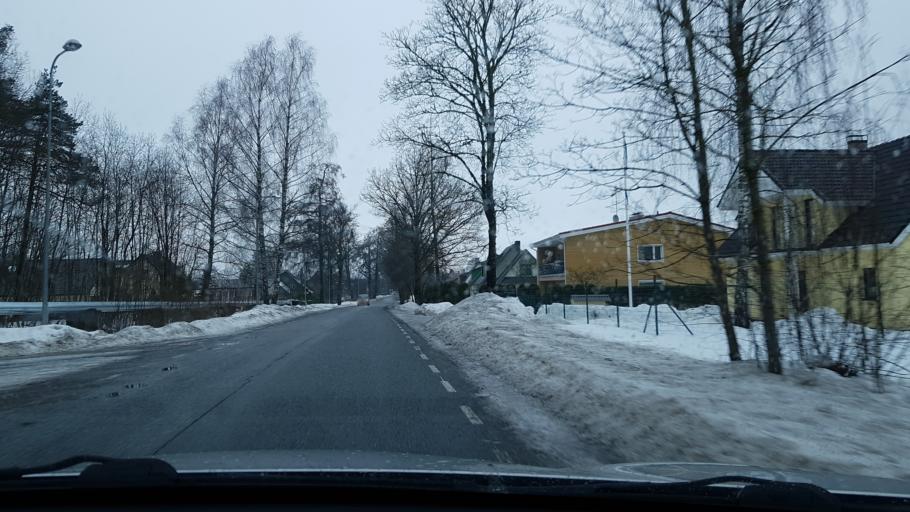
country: EE
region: Raplamaa
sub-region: Maerjamaa vald
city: Marjamaa
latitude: 58.8967
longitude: 24.4316
